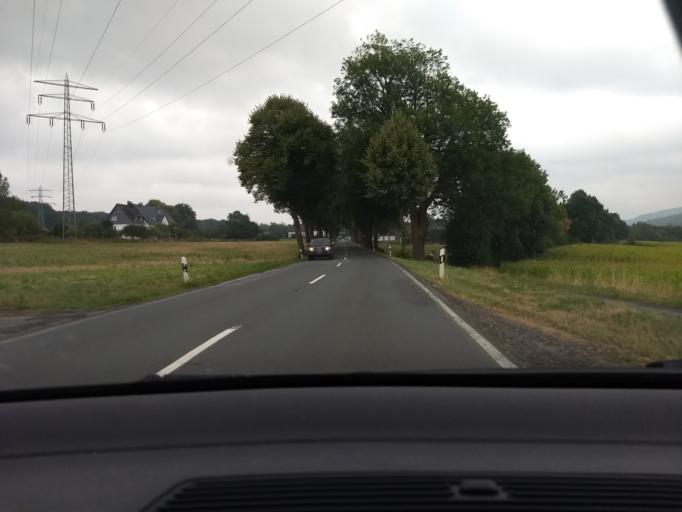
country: DE
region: North Rhine-Westphalia
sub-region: Regierungsbezirk Arnsberg
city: Arnsberg
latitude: 51.3628
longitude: 8.1791
